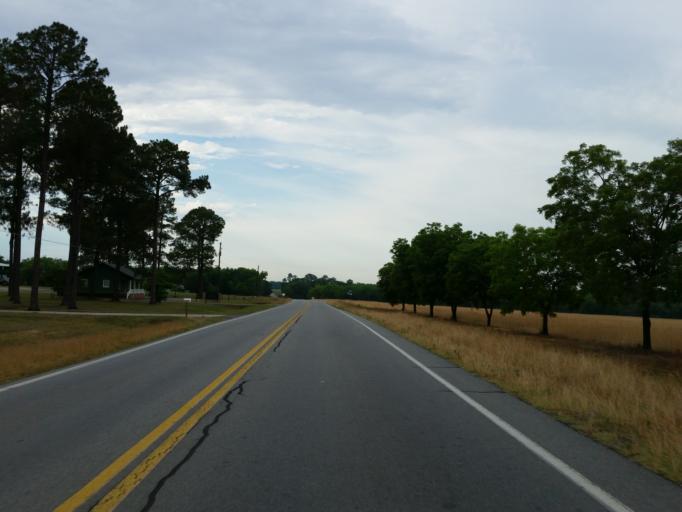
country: US
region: Georgia
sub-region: Dooly County
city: Vienna
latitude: 32.0322
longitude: -83.7922
